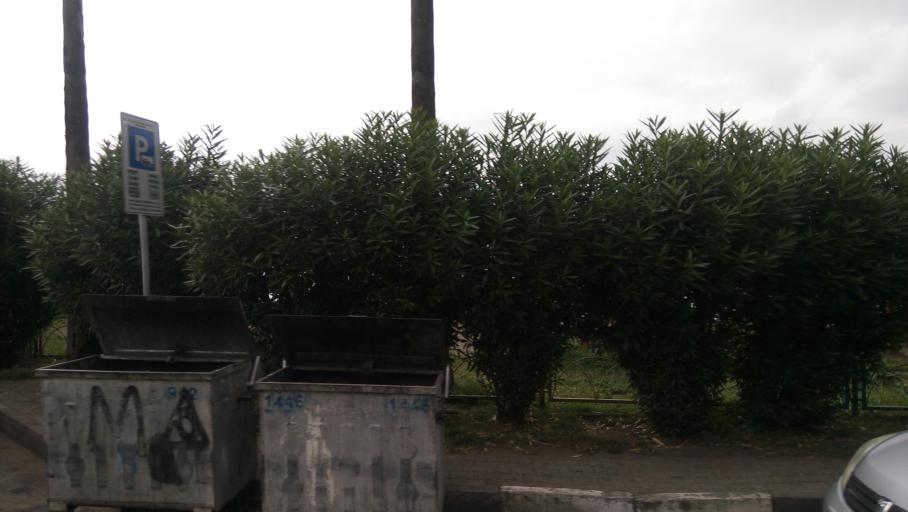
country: GE
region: Ajaria
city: Batumi
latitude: 41.6468
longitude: 41.6463
